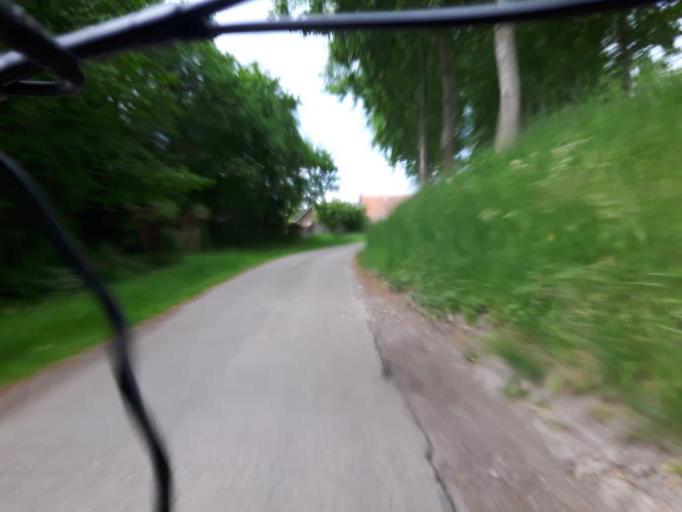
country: NL
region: Zeeland
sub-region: Gemeente Borsele
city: Borssele
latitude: 51.4346
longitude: 3.8040
